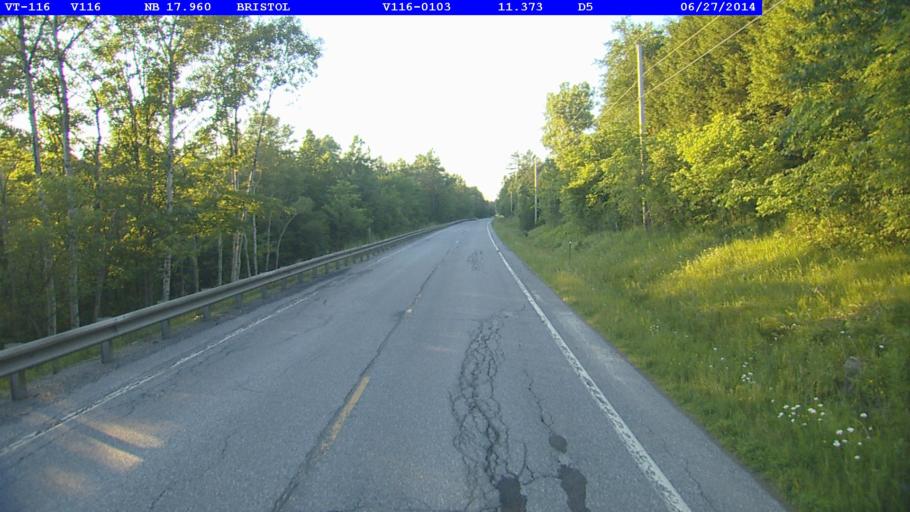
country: US
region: Vermont
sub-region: Addison County
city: Bristol
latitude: 44.1728
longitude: -73.0567
